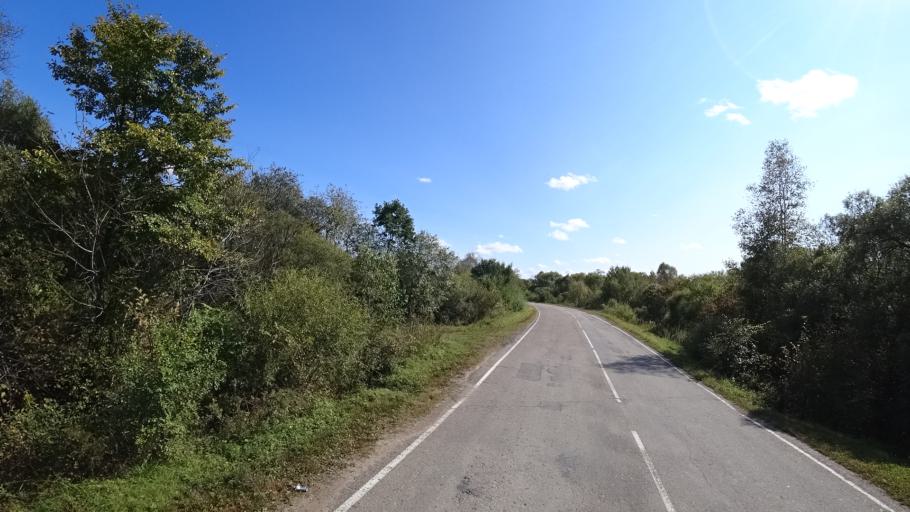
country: RU
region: Amur
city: Arkhara
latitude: 49.4017
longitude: 130.1296
